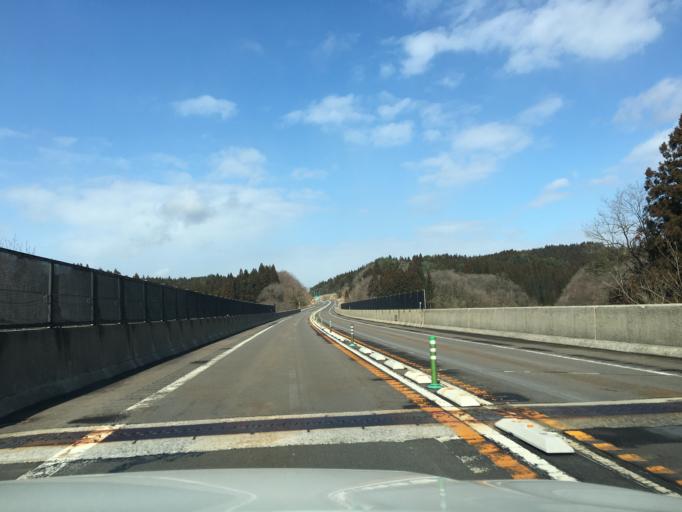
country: JP
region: Akita
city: Akita
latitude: 39.7442
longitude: 140.1605
